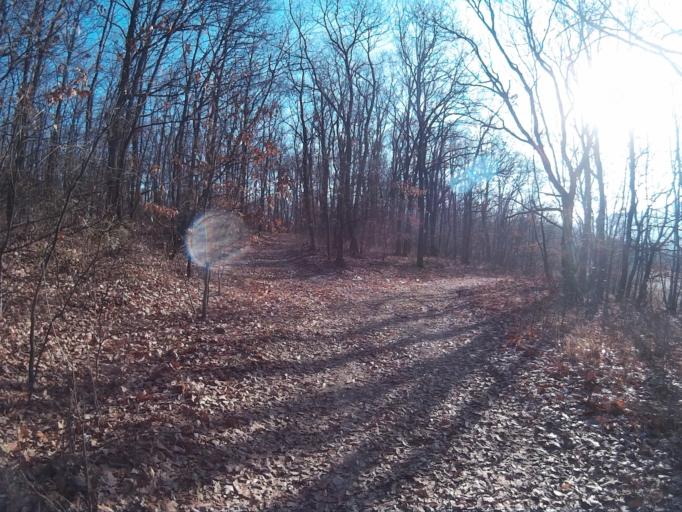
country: HU
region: Nograd
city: Bercel
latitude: 47.9098
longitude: 19.4069
